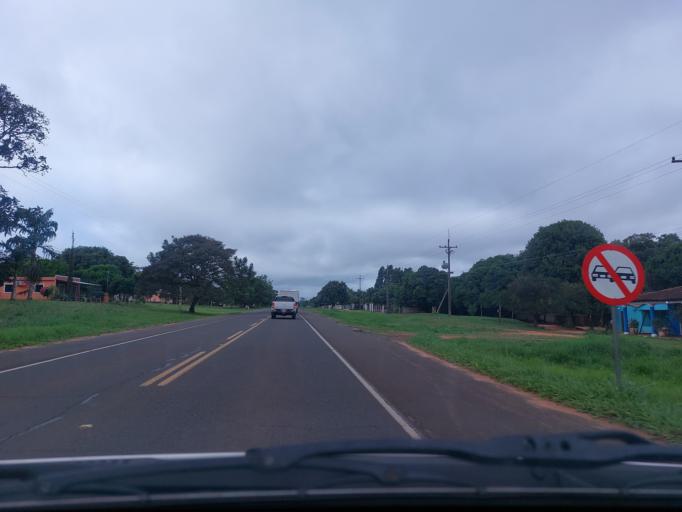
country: PY
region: San Pedro
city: Guayaybi
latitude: -24.6319
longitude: -56.3787
